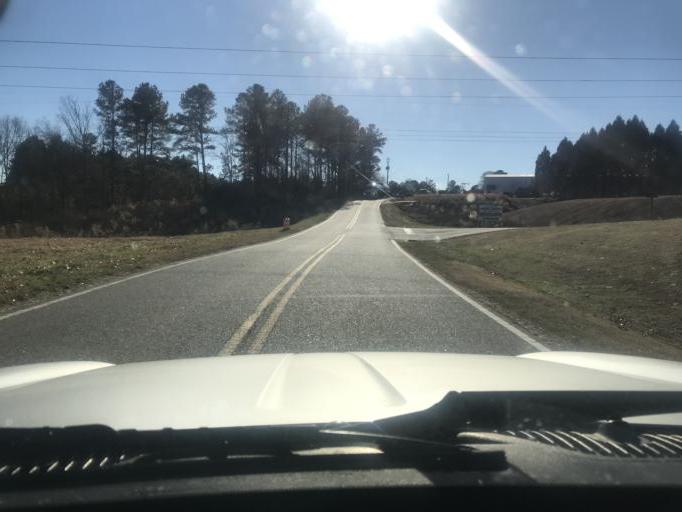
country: US
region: Georgia
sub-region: Barrow County
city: Winder
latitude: 33.9977
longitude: -83.7594
